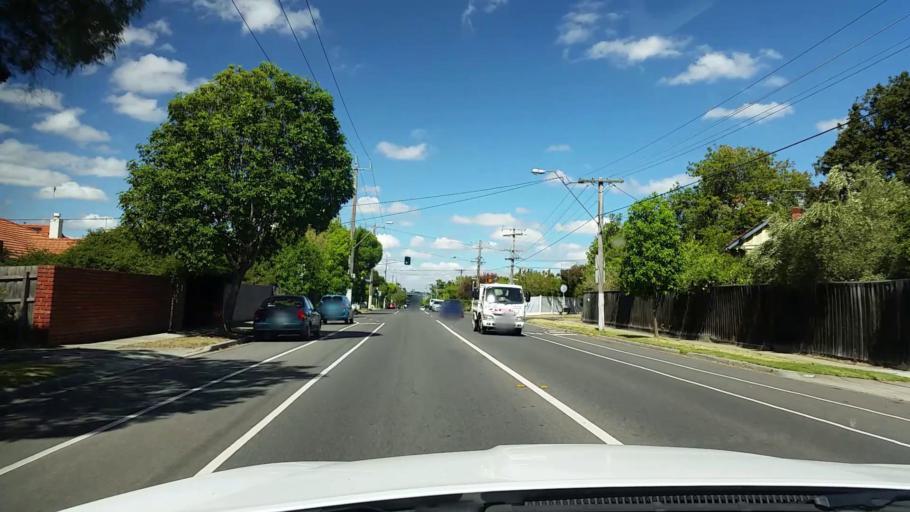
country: AU
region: Victoria
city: Carnegie
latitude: -37.8734
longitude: 145.0639
